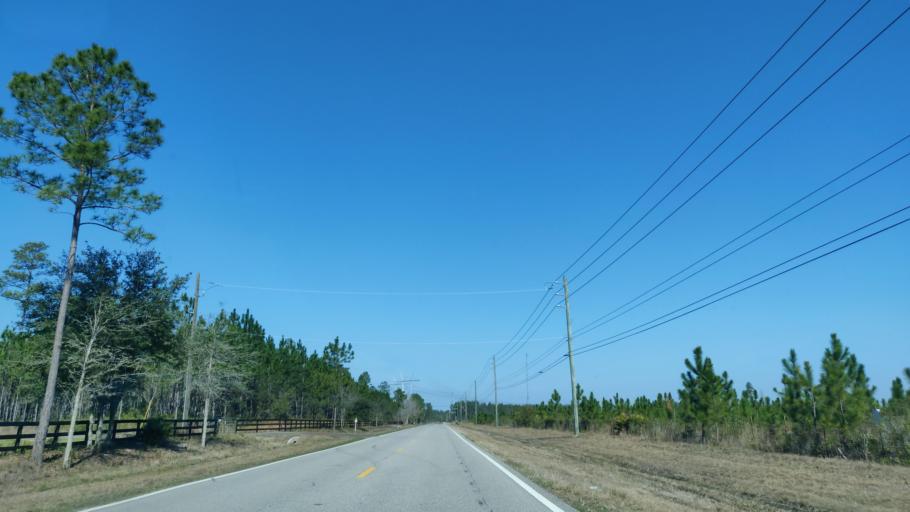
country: US
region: Florida
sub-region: Duval County
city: Baldwin
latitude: 30.2570
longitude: -81.9508
